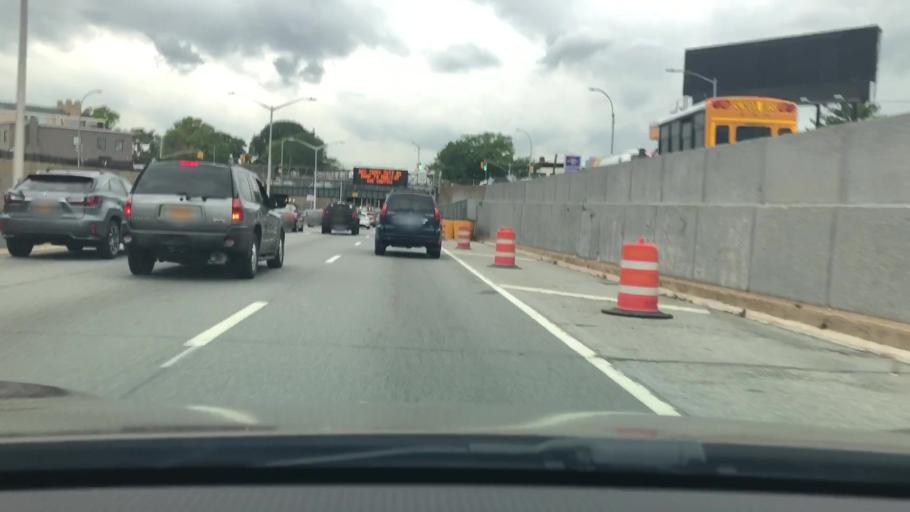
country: US
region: New York
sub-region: Queens County
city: Long Island City
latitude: 40.7674
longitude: -73.9001
